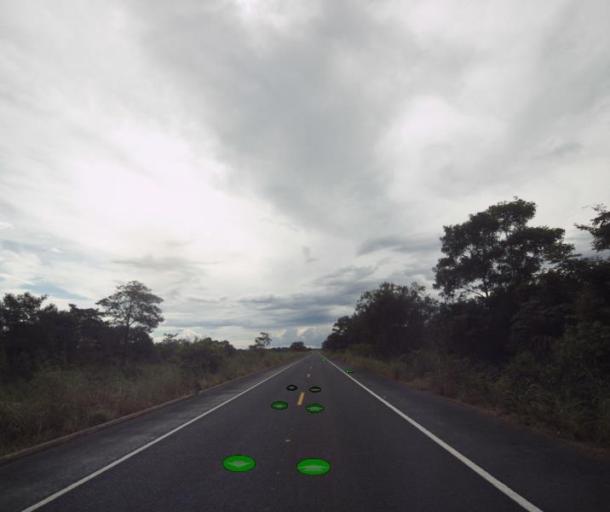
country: BR
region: Goias
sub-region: Sao Miguel Do Araguaia
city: Sao Miguel do Araguaia
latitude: -13.2493
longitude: -50.5308
